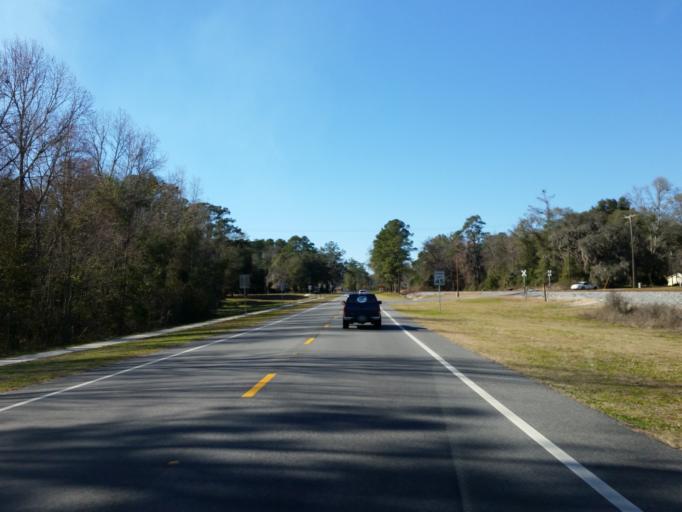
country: US
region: Florida
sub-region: Suwannee County
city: Wellborn
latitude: 30.3273
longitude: -82.7413
